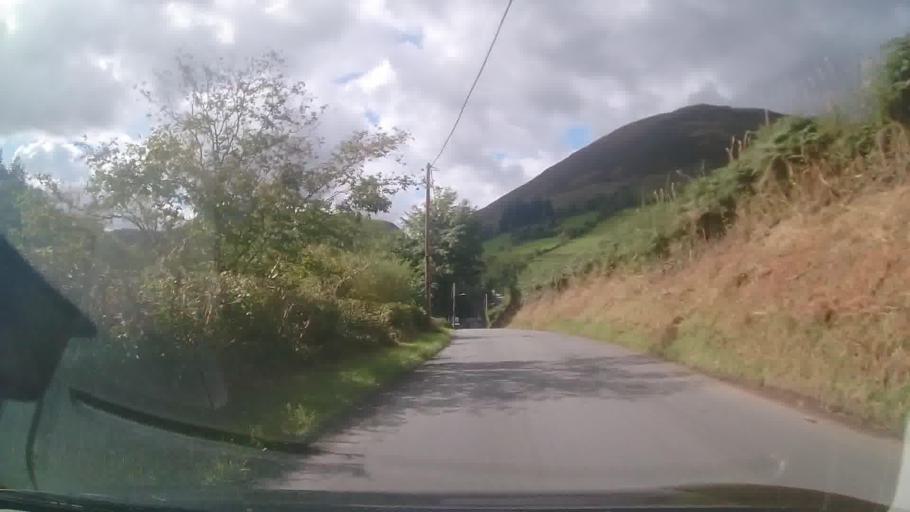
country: GB
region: Wales
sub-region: Gwynedd
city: Corris
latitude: 52.7280
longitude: -3.6751
